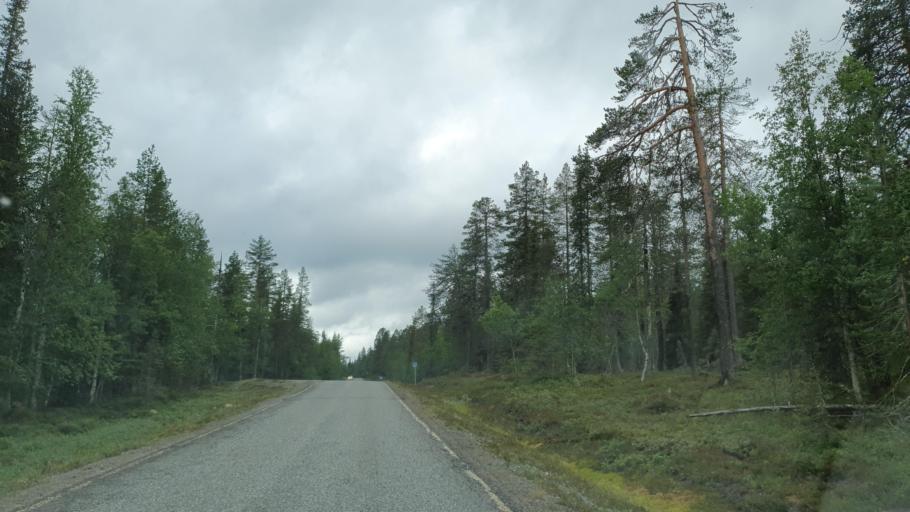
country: FI
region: Lapland
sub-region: Tunturi-Lappi
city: Muonio
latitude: 67.7287
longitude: 24.2490
